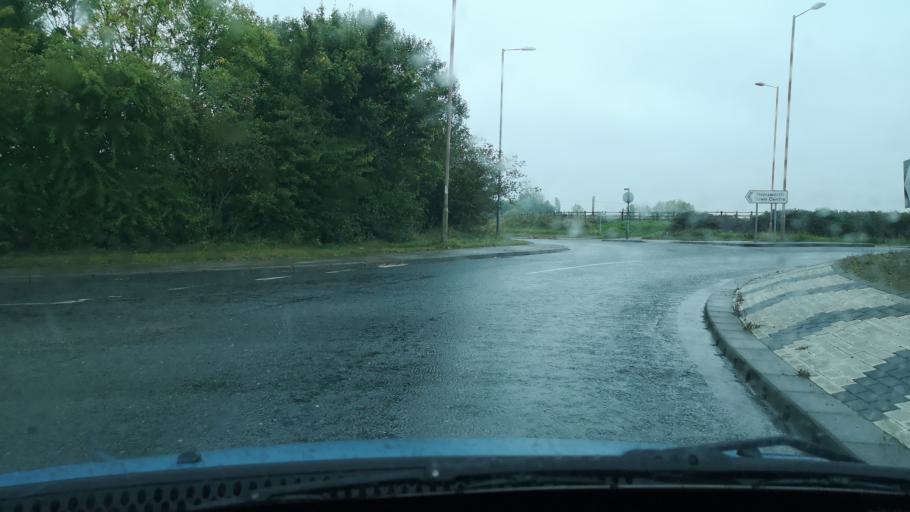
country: GB
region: England
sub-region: City and Borough of Wakefield
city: Hemsworth
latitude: 53.6275
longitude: -1.3381
